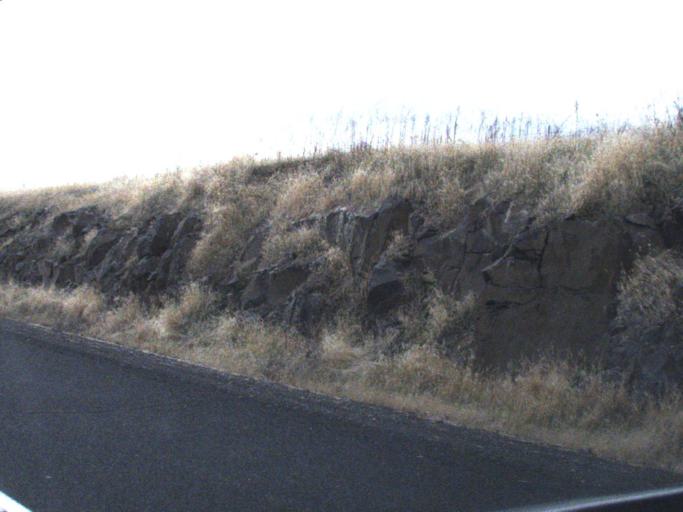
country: US
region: Washington
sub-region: Adams County
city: Ritzville
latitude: 46.7470
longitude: -118.2017
